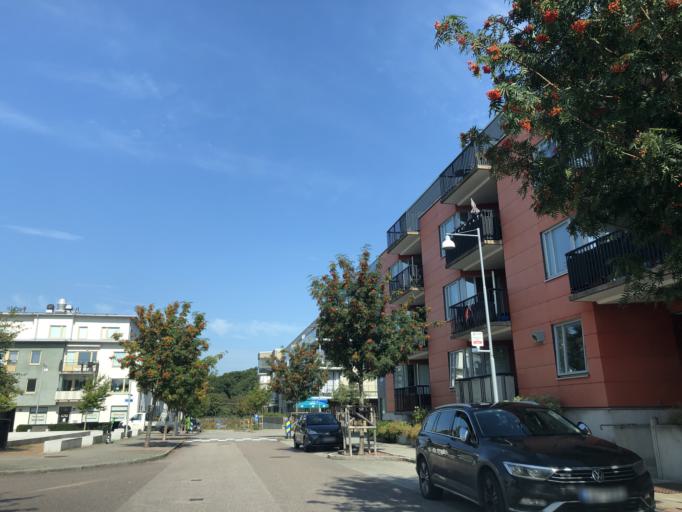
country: SE
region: Vaestra Goetaland
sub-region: Goteborg
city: Majorna
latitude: 57.6990
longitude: 11.9059
